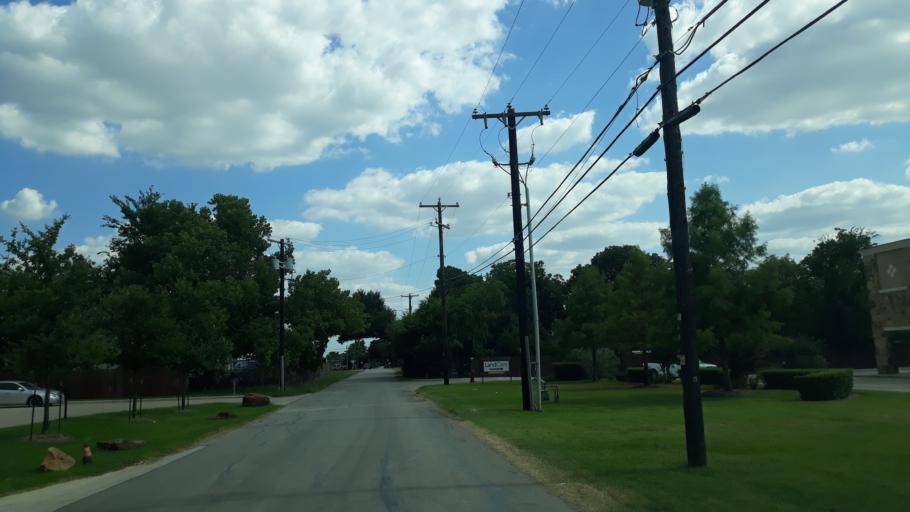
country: US
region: Texas
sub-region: Dallas County
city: Irving
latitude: 32.8124
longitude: -97.0058
